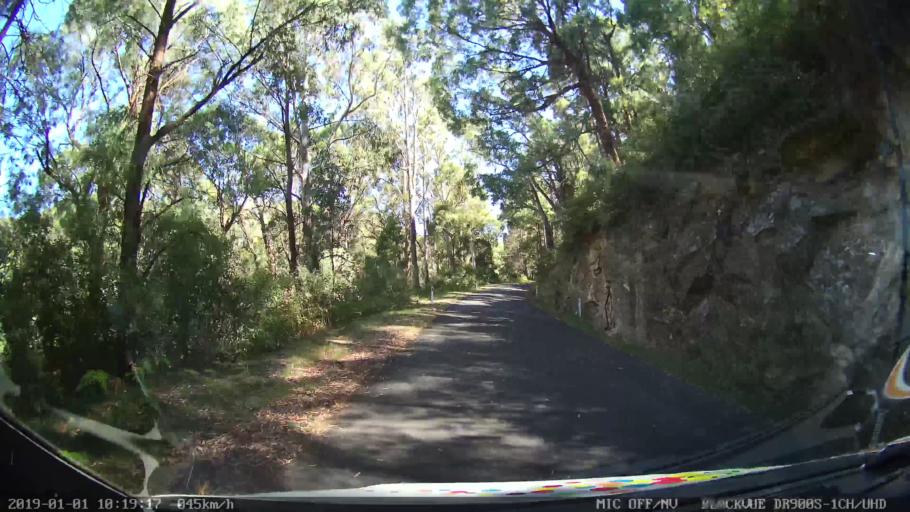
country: AU
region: New South Wales
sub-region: Snowy River
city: Jindabyne
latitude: -36.0855
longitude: 148.1858
